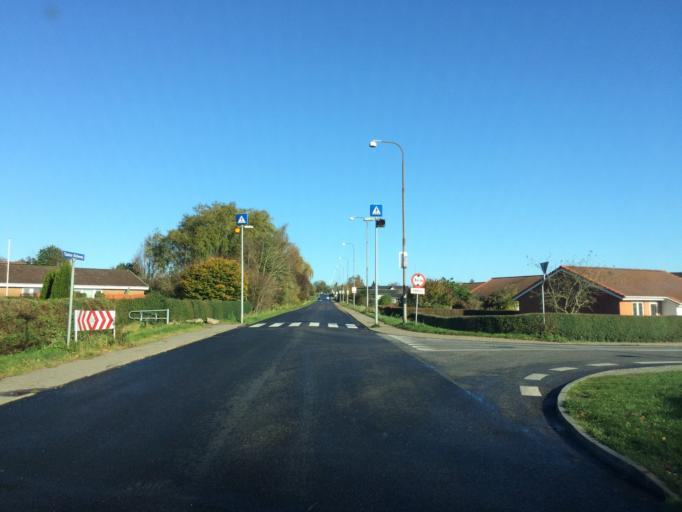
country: DK
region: South Denmark
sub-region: Fredericia Kommune
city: Taulov
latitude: 55.5344
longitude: 9.6039
